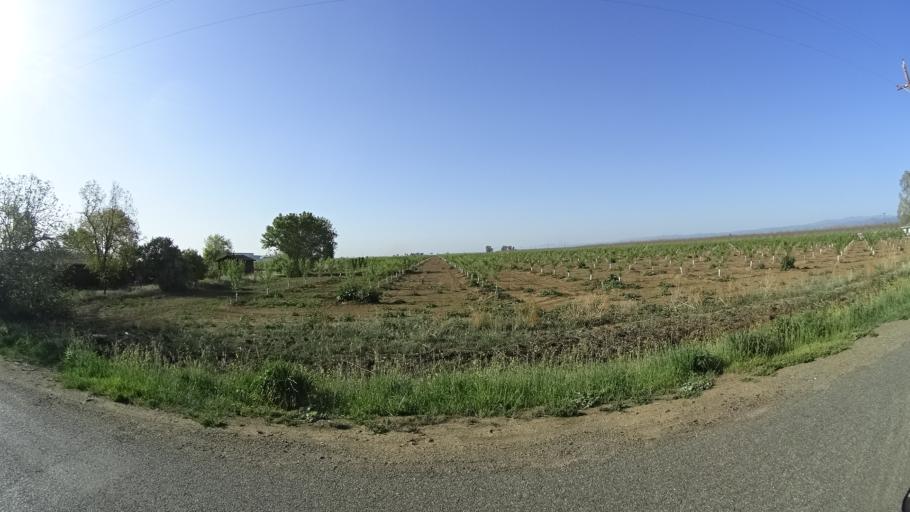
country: US
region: California
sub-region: Glenn County
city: Willows
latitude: 39.5095
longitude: -122.2381
